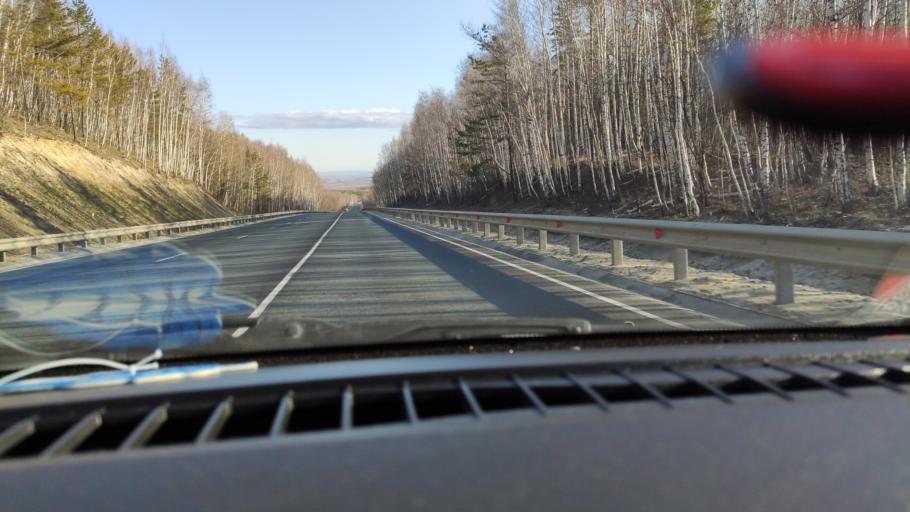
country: RU
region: Saratov
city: Khvalynsk
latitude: 52.5029
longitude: 48.0152
